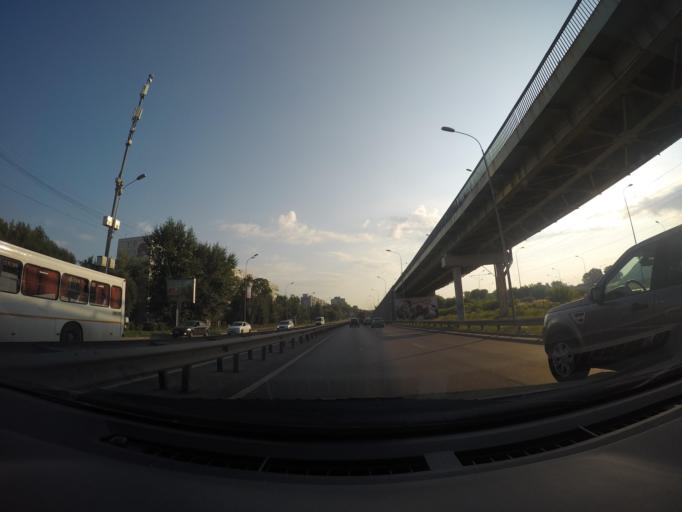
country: RU
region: Moskovskaya
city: Lyubertsy
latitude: 55.6659
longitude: 37.8814
